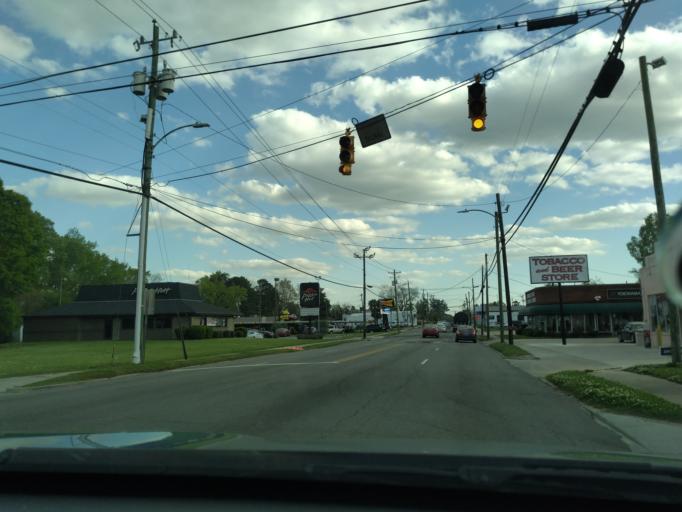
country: US
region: South Carolina
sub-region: Williamsburg County
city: Kingstree
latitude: 33.6670
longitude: -79.8347
